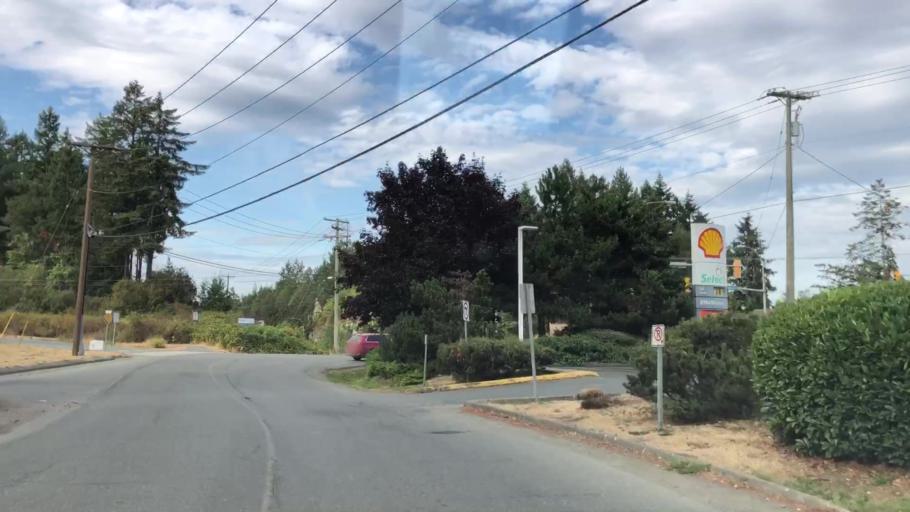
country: CA
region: British Columbia
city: North Saanich
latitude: 48.6519
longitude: -123.5607
